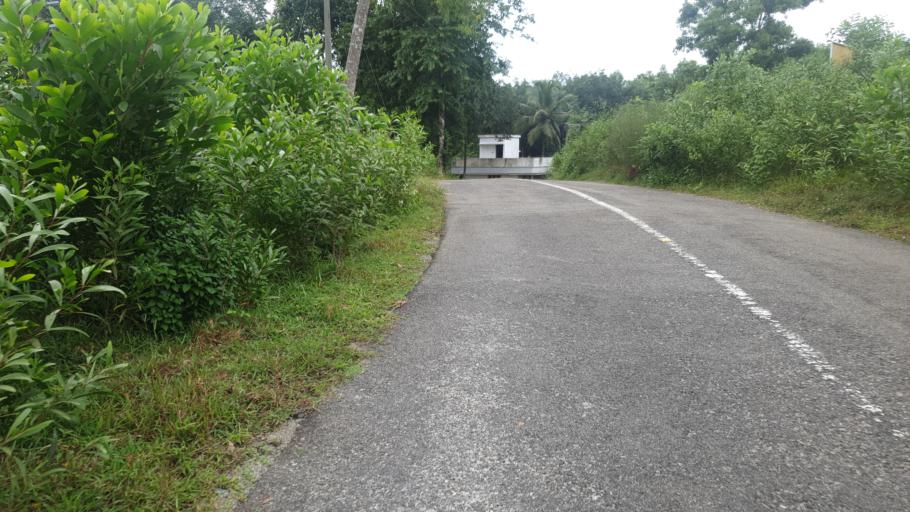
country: IN
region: Kerala
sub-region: Thiruvananthapuram
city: Nedumangad
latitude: 8.6388
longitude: 77.1092
